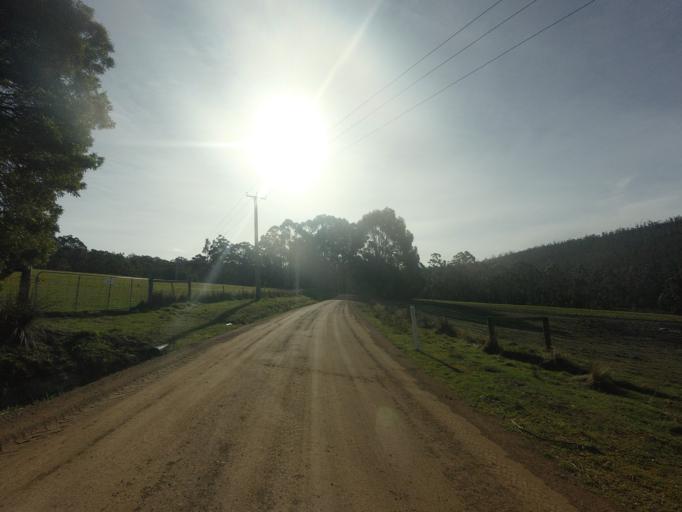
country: AU
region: Tasmania
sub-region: Kingborough
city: Kettering
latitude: -43.0987
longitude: 147.2632
